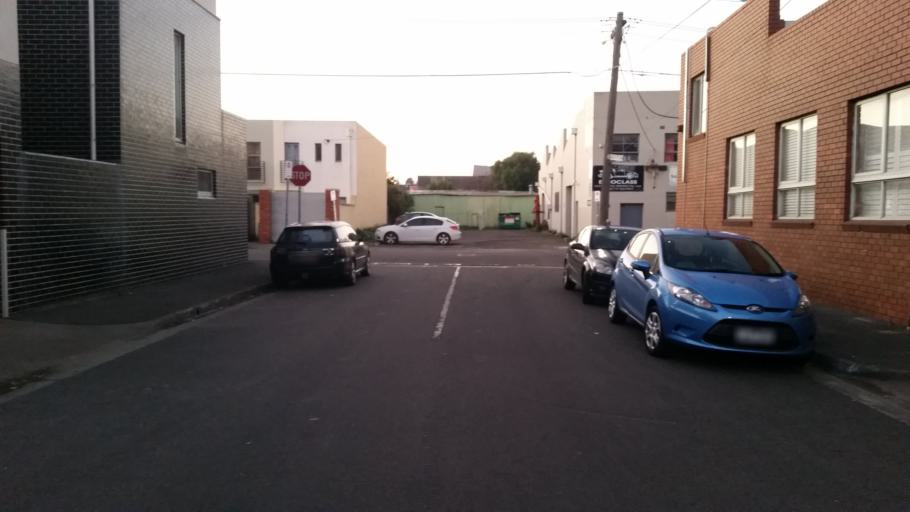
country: AU
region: Victoria
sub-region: Yarra
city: Richmond
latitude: -37.8166
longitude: 145.0110
